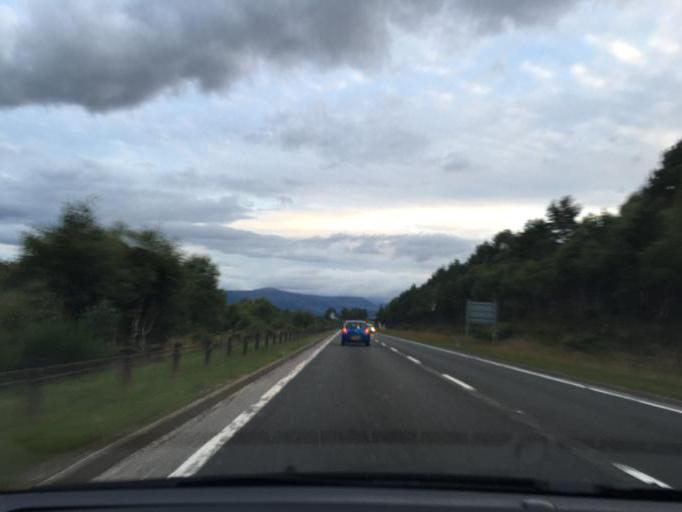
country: GB
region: Scotland
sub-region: Highland
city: Aviemore
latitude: 57.2394
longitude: -3.8083
